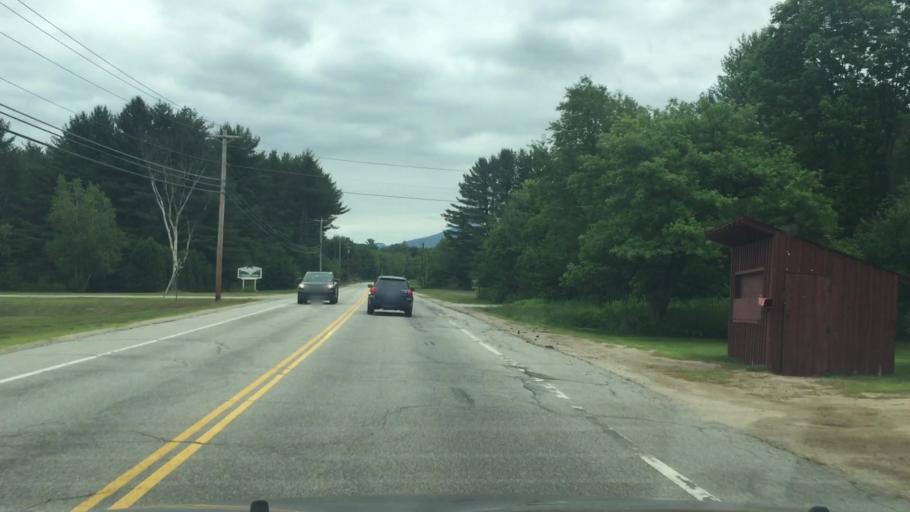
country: US
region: New Hampshire
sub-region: Carroll County
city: North Conway
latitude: 44.0796
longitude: -71.2585
